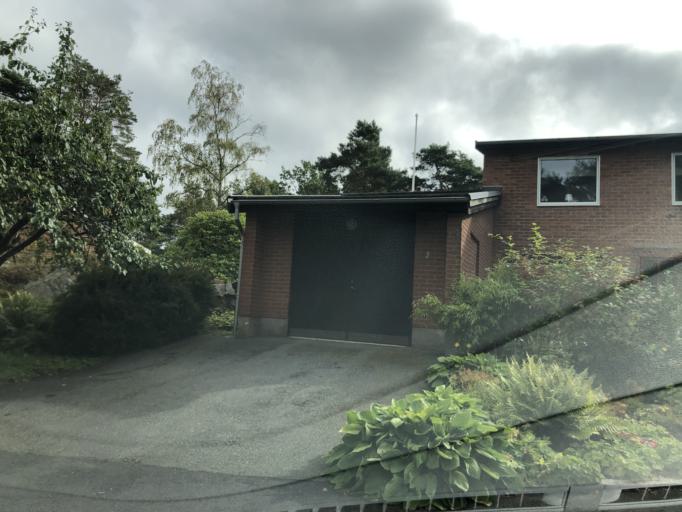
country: SE
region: Vaestra Goetaland
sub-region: Goteborg
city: Majorna
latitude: 57.7391
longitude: 11.9111
